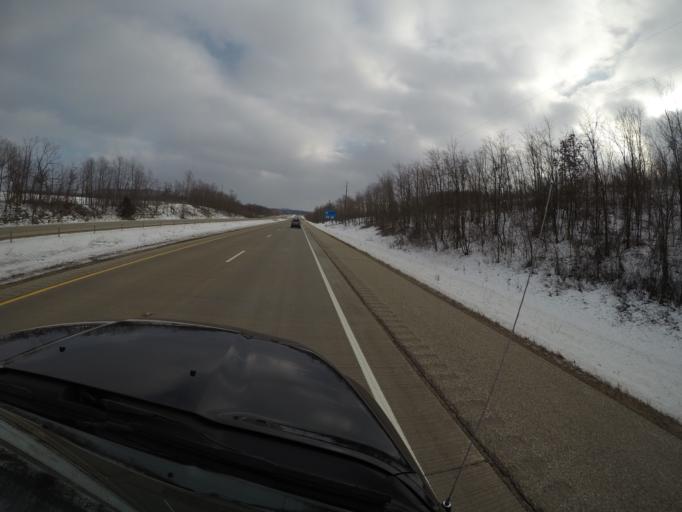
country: US
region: Wisconsin
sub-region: La Crosse County
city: Holmen
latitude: 43.9501
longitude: -91.2715
